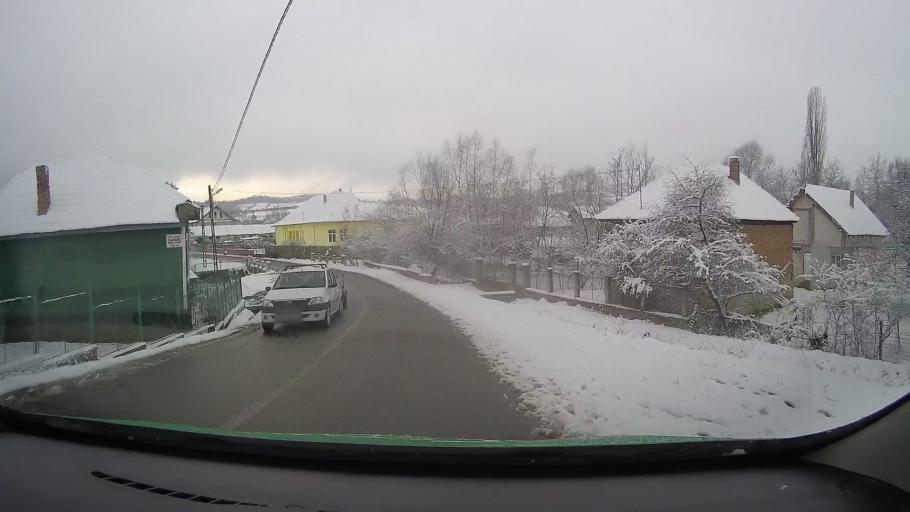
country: RO
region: Hunedoara
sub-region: Oras Hateg
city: Hateg
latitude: 45.6543
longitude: 22.9237
